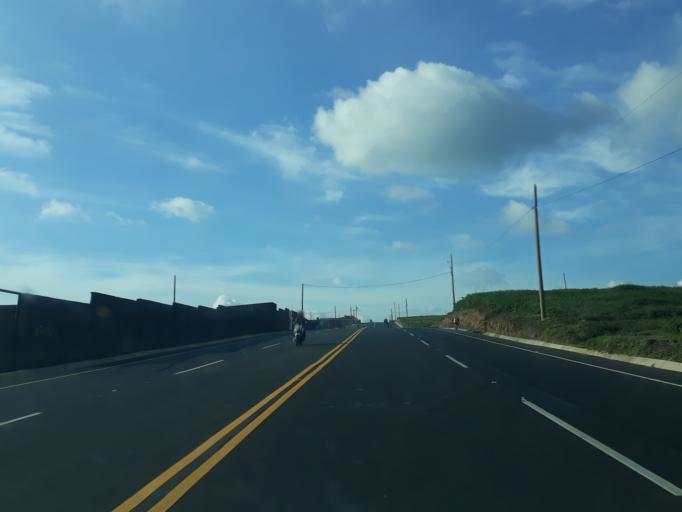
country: NI
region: Managua
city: El Crucero
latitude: 11.9514
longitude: -86.3011
